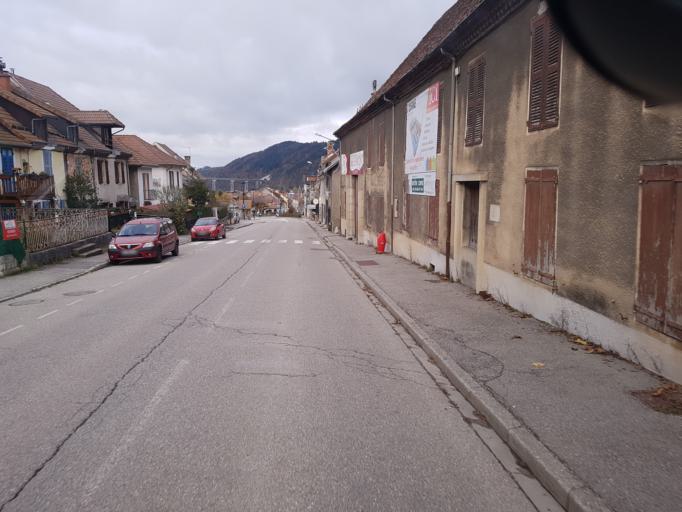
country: FR
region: Rhone-Alpes
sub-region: Departement de l'Isere
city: La Motte-Saint-Martin
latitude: 44.9146
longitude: 5.6338
